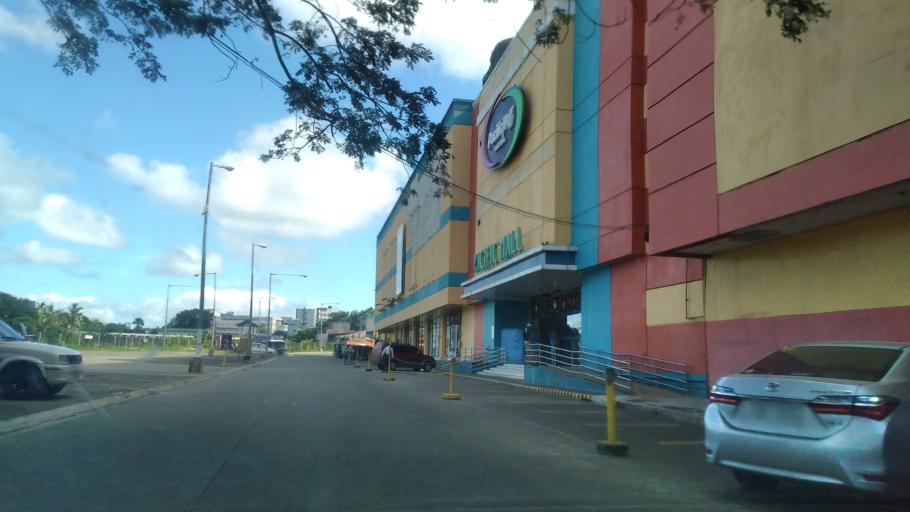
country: PH
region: Calabarzon
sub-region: Province of Quezon
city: Lucena
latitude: 13.9373
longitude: 121.6085
